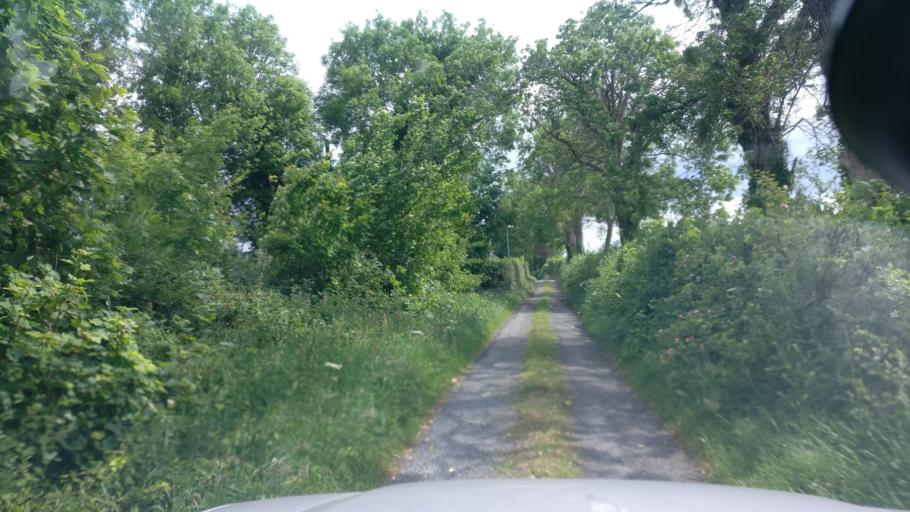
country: IE
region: Connaught
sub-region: County Galway
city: Ballinasloe
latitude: 53.2710
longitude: -8.3330
